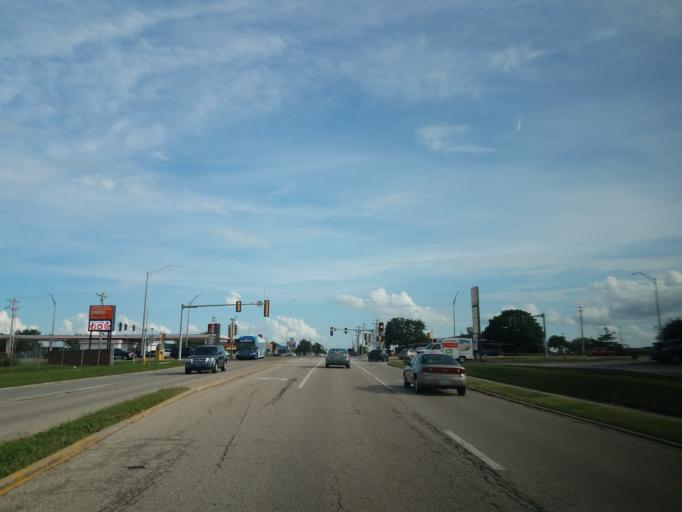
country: US
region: Illinois
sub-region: McLean County
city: Bloomington
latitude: 40.4893
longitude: -88.9432
